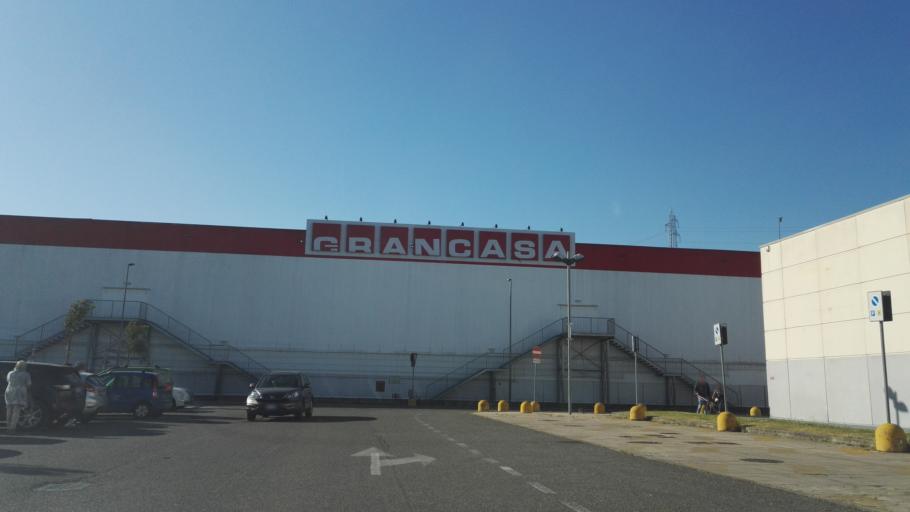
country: IT
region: Lombardy
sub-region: Citta metropolitana di Milano
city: San Giuliano Milanese
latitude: 45.3799
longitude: 9.3046
